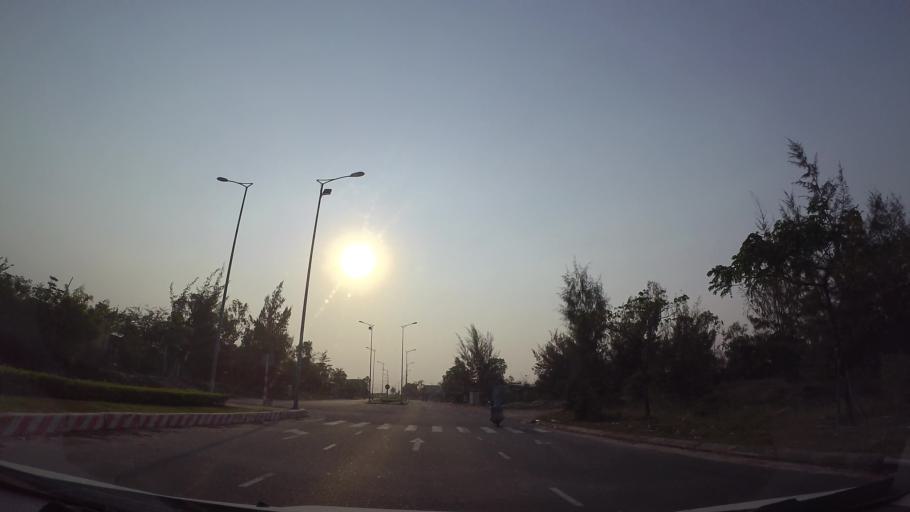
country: VN
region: Da Nang
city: Ngu Hanh Son
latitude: 15.9779
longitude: 108.2407
